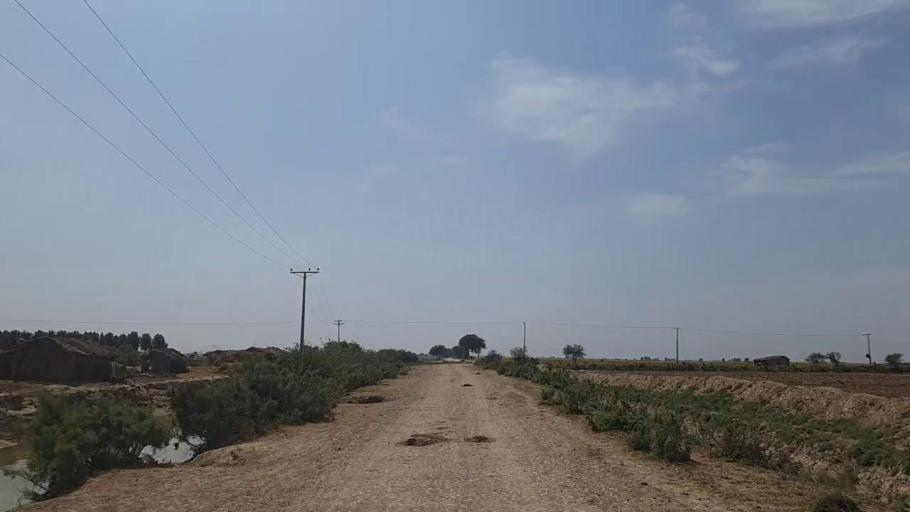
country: PK
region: Sindh
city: Jati
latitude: 24.5325
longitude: 68.2925
